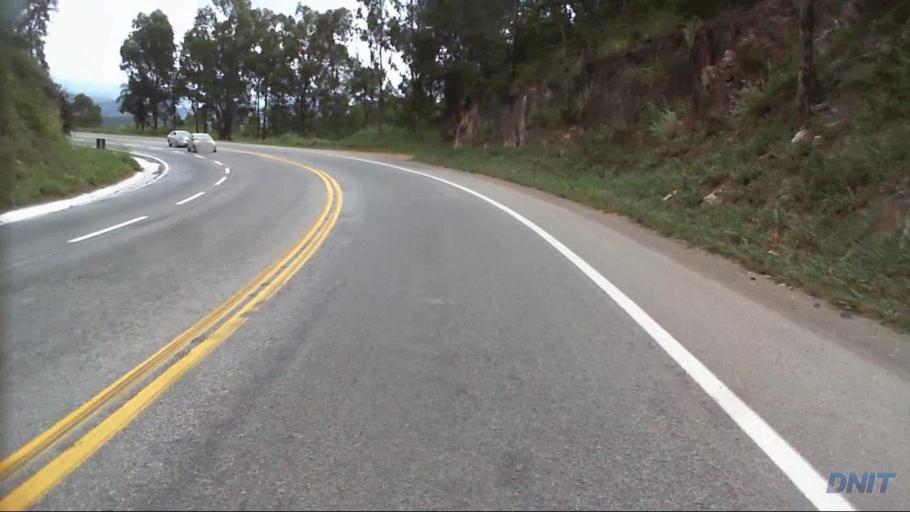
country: BR
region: Minas Gerais
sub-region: Caete
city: Caete
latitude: -19.7869
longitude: -43.7000
